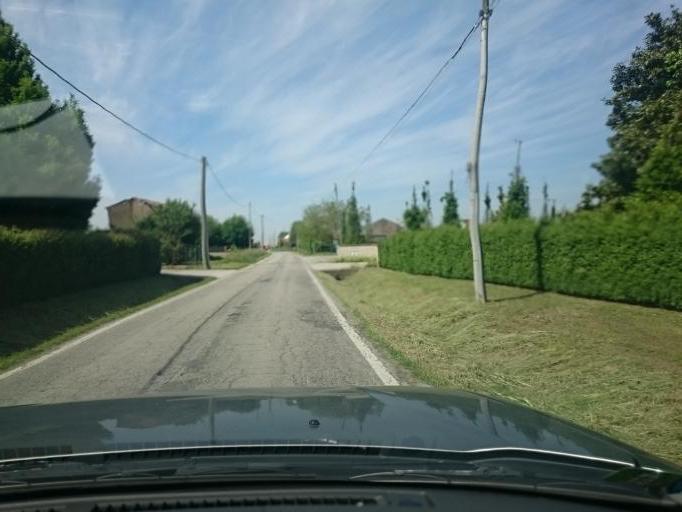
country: IT
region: Veneto
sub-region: Provincia di Padova
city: Cartura
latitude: 45.2547
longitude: 11.8442
